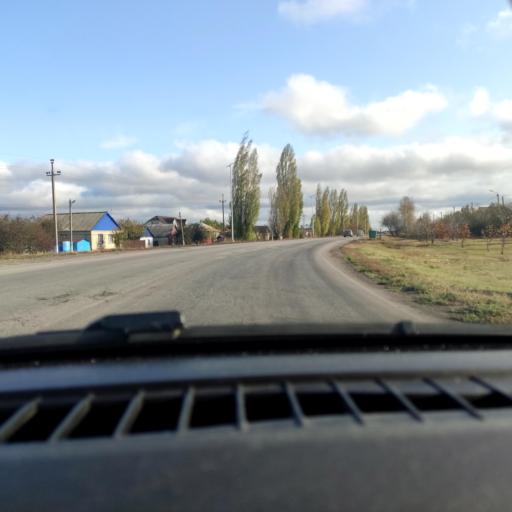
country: RU
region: Belgorod
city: Ilovka
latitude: 50.7299
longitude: 38.6830
